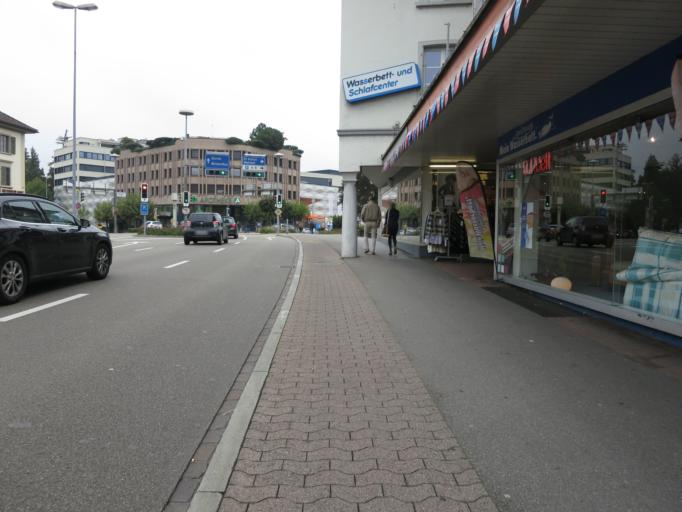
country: CH
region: Saint Gallen
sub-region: Wahlkreis See-Gaster
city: Rapperswil
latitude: 47.2282
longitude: 8.8198
